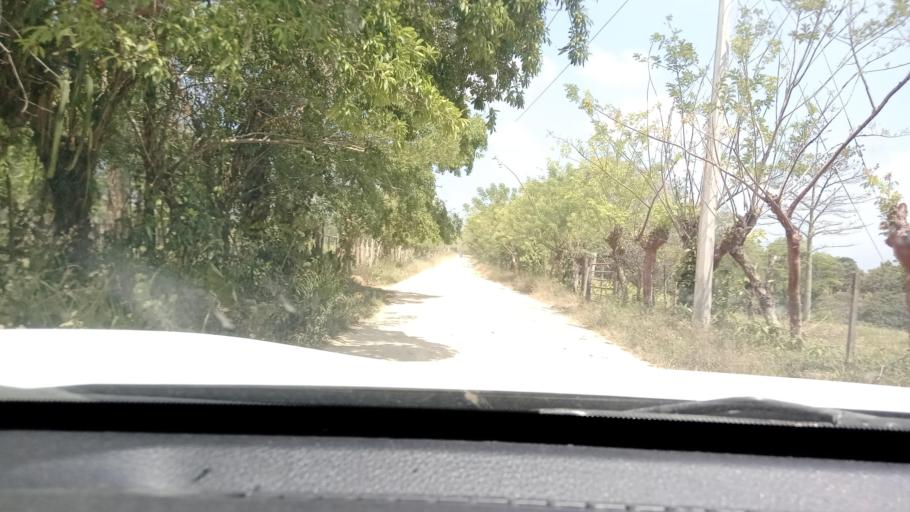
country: MX
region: Veracruz
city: Las Choapas
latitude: 17.9400
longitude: -94.1203
